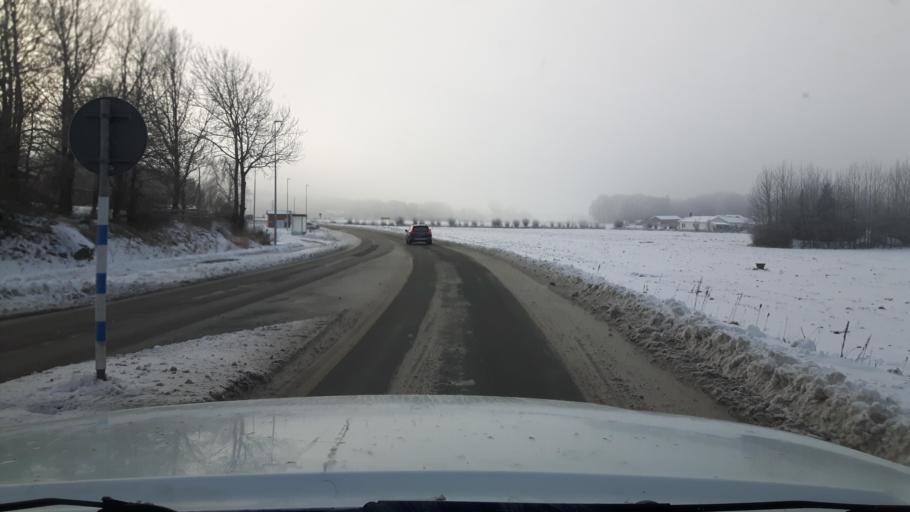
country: SE
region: Halland
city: Saro
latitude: 57.4291
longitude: 11.9361
